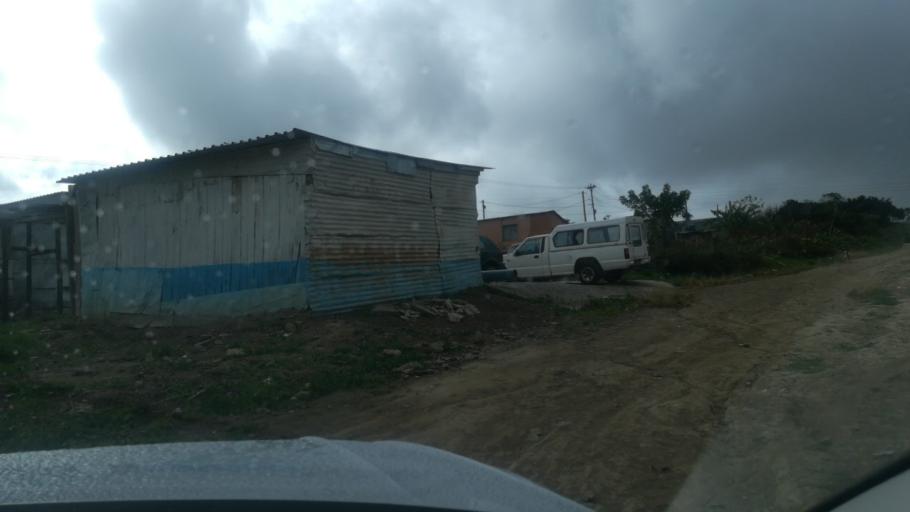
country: ZA
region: Eastern Cape
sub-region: Buffalo City Metropolitan Municipality
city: East London
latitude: -32.9949
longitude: 27.7977
